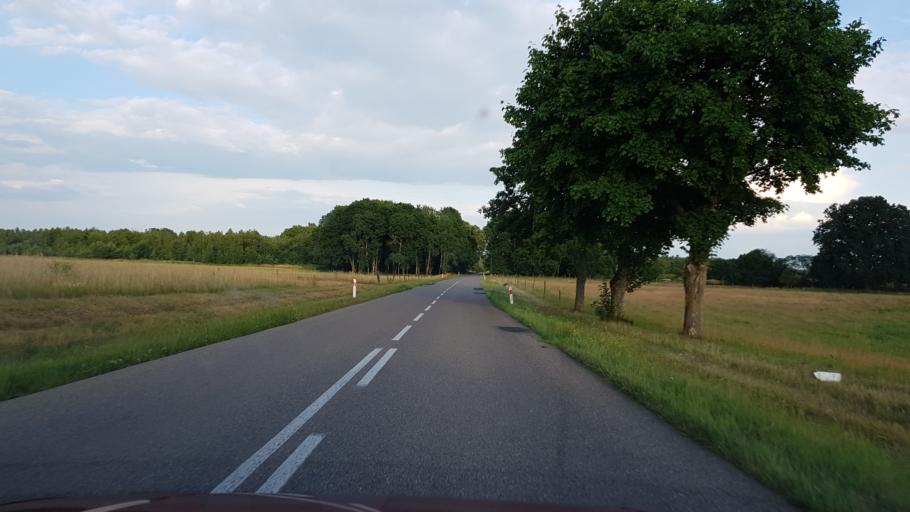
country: PL
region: West Pomeranian Voivodeship
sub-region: Powiat goleniowski
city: Nowogard
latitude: 53.6958
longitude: 15.0612
